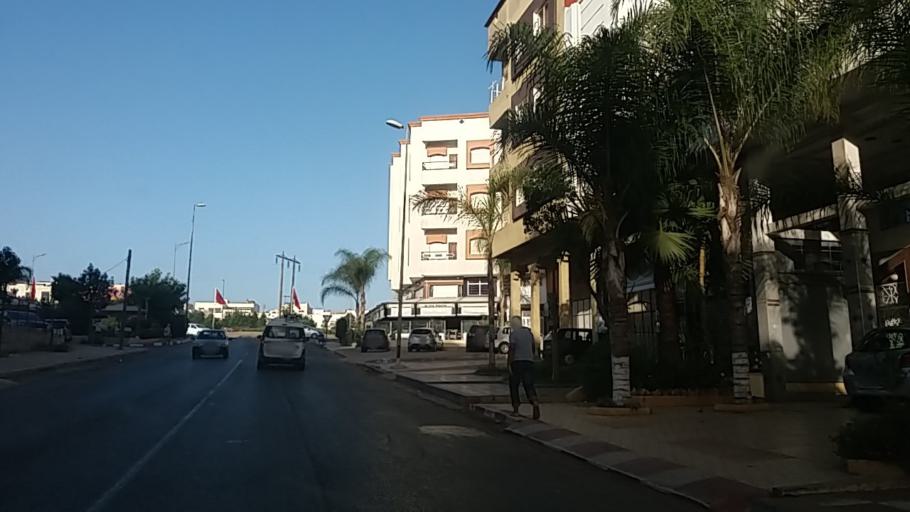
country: MA
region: Gharb-Chrarda-Beni Hssen
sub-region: Kenitra Province
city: Kenitra
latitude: 34.2557
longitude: -6.6144
